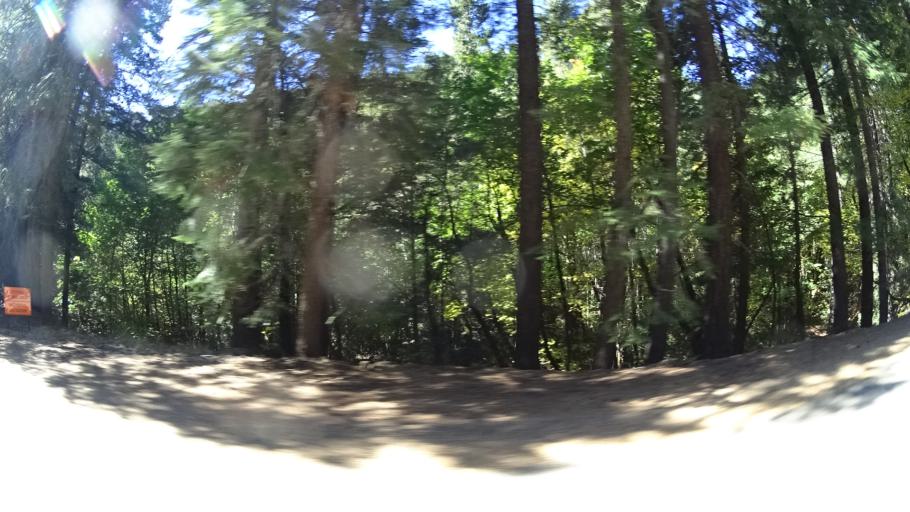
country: US
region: California
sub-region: Siskiyou County
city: Yreka
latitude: 41.3746
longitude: -123.0200
